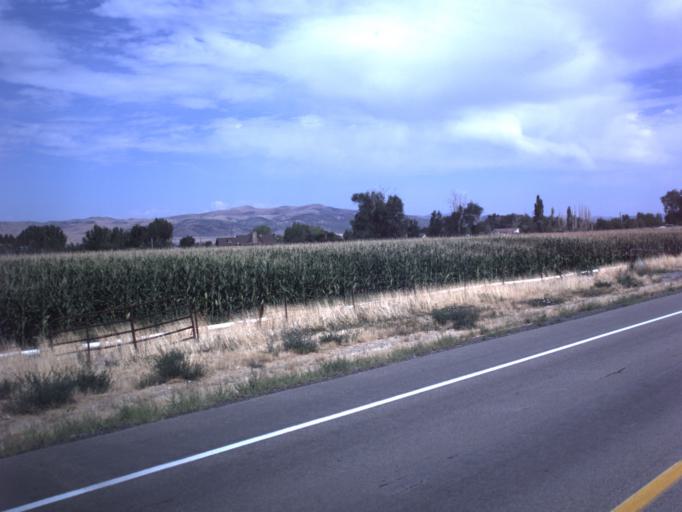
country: US
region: Utah
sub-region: Juab County
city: Nephi
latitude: 39.5479
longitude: -111.8638
